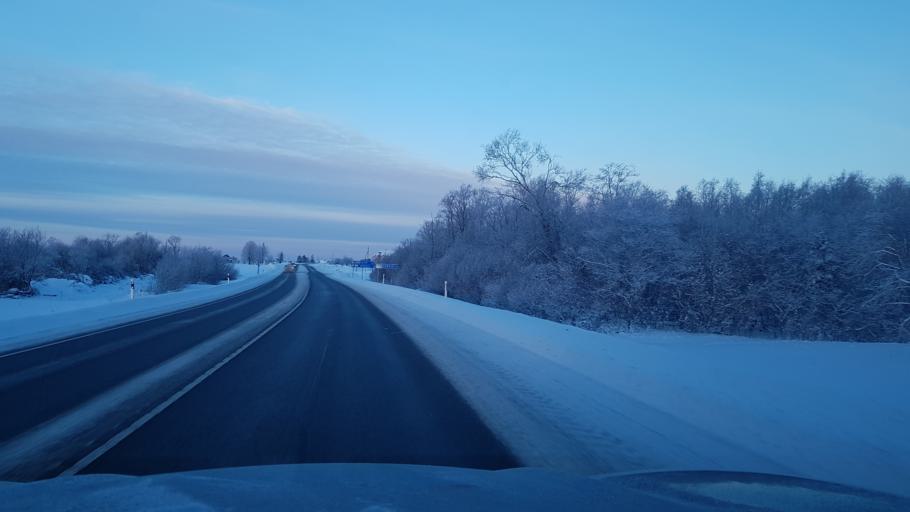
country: EE
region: Ida-Virumaa
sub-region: Narva-Joesuu linn
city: Narva-Joesuu
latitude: 59.4005
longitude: 28.0678
